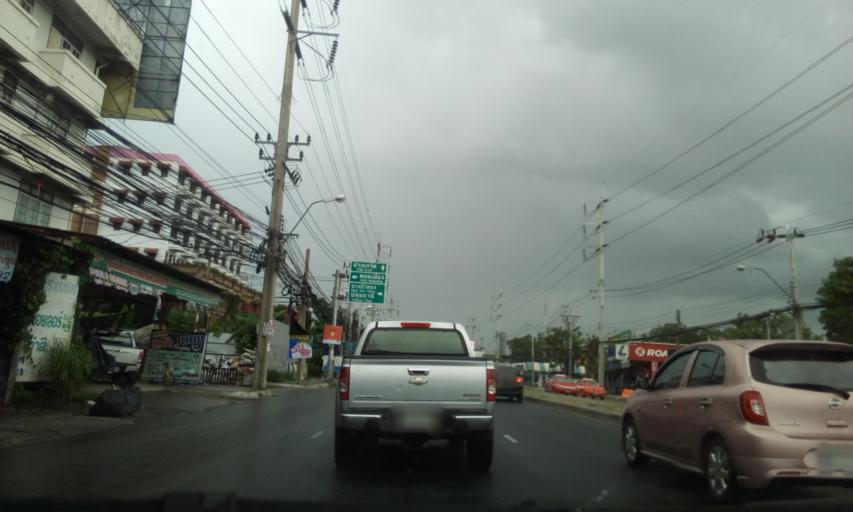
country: TH
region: Nonthaburi
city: Pak Kret
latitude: 13.9437
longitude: 100.5438
